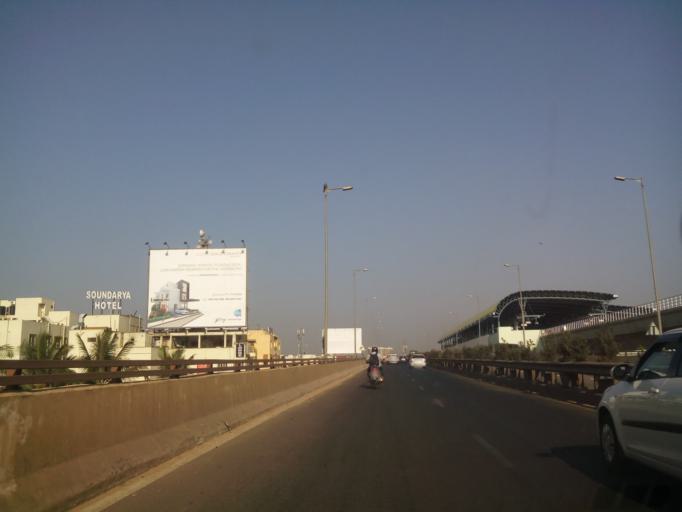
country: IN
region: Karnataka
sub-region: Bangalore Urban
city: Yelahanka
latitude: 13.0426
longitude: 77.5140
